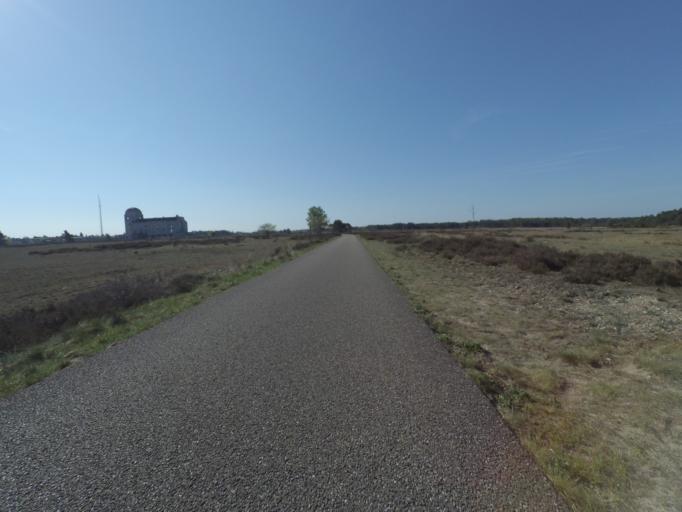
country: NL
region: Gelderland
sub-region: Gemeente Ede
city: Harskamp
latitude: 52.1753
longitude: 5.8157
